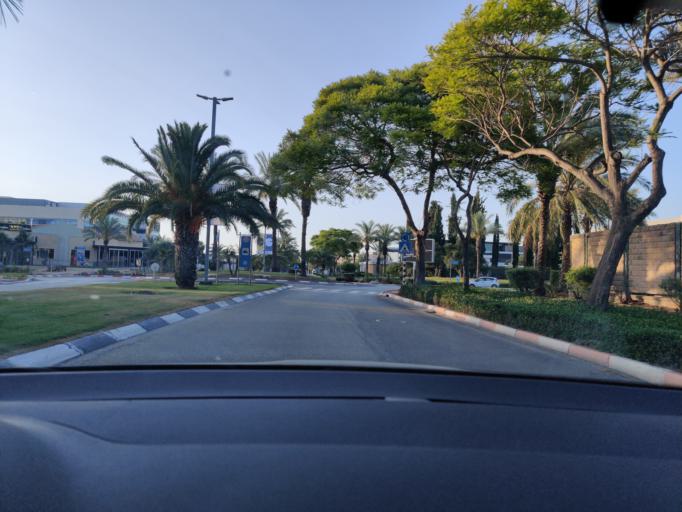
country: IL
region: Haifa
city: Qesarya
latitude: 32.4835
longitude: 34.9482
